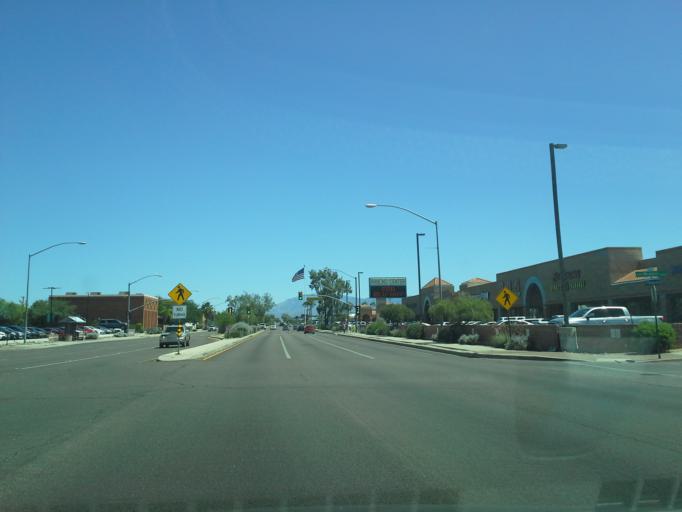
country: US
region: Arizona
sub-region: Pima County
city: Tucson
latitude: 32.2361
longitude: -110.9232
